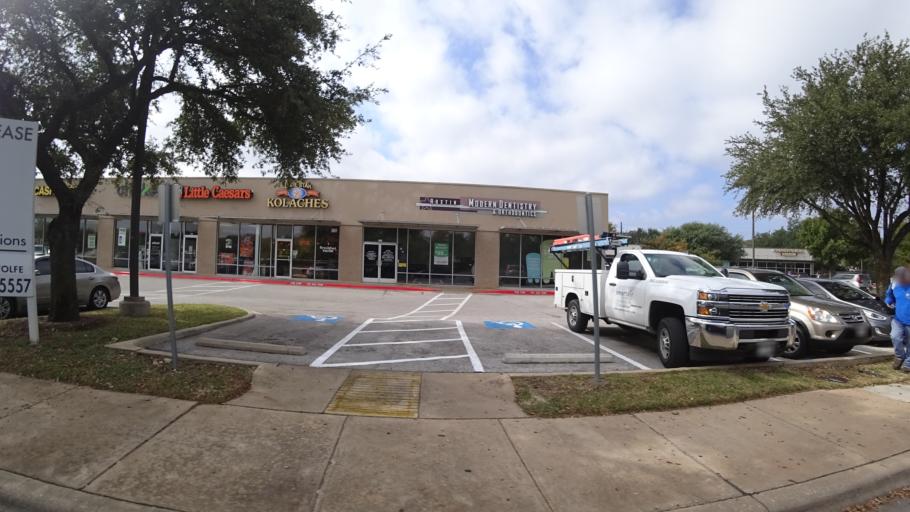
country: US
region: Texas
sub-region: Travis County
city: Shady Hollow
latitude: 30.2156
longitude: -97.8333
